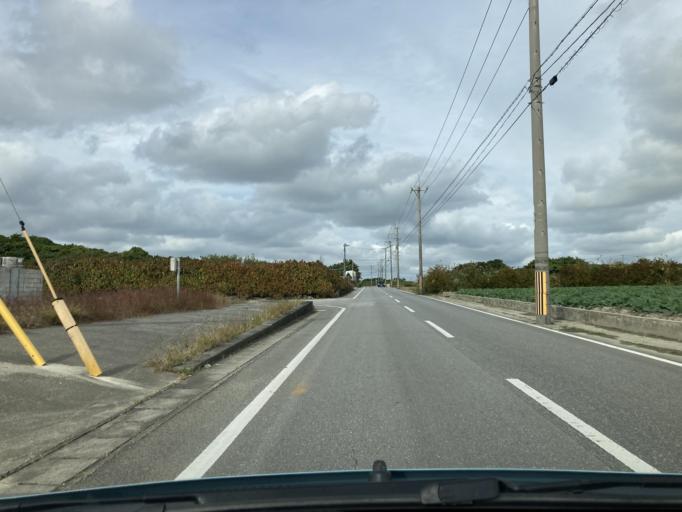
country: JP
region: Okinawa
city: Itoman
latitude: 26.1094
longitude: 127.6885
